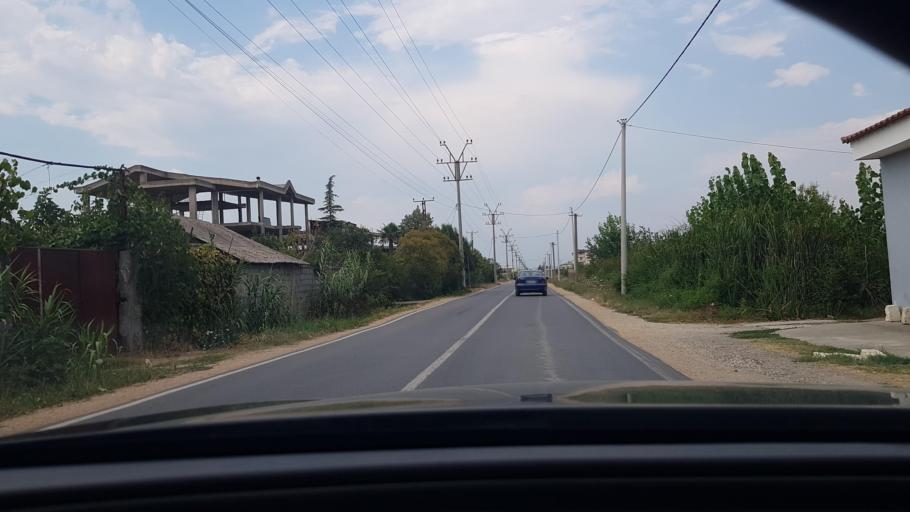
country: AL
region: Durres
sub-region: Rrethi i Durresit
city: Sukth
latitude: 41.4024
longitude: 19.5467
